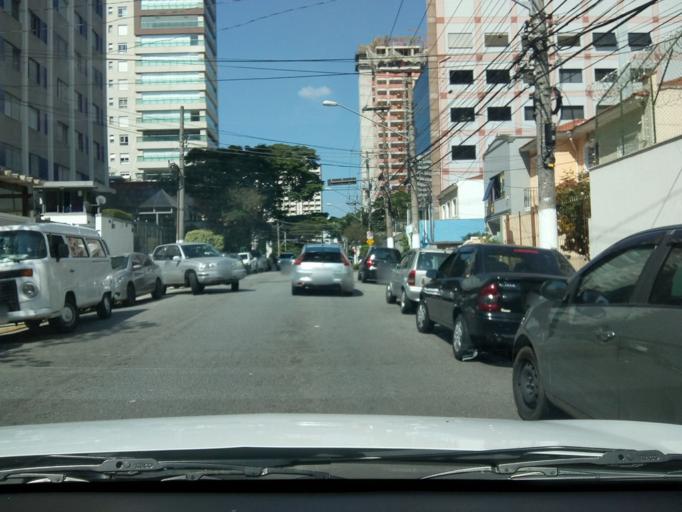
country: BR
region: Sao Paulo
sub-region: Sao Paulo
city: Sao Paulo
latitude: -23.5766
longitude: -46.6476
